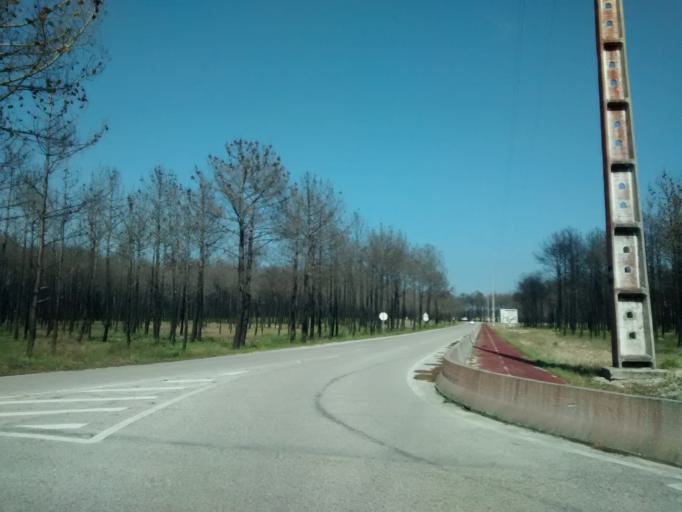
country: PT
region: Coimbra
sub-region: Figueira da Foz
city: Lavos
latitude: 40.0006
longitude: -8.8680
